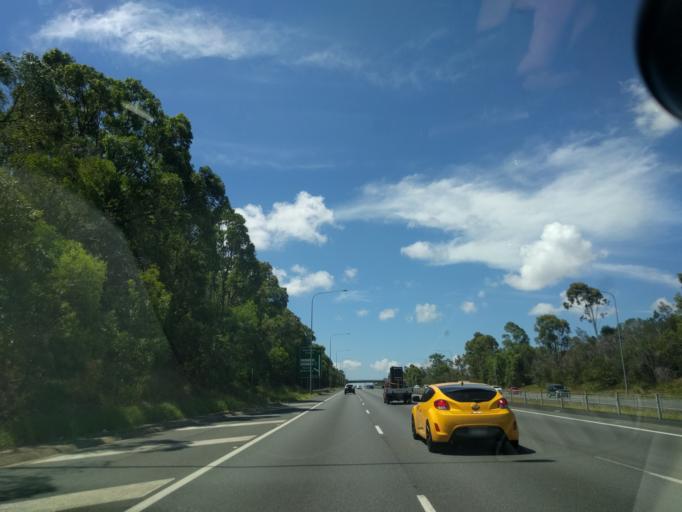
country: AU
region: Queensland
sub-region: Moreton Bay
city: Murrumba Downs
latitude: -27.2656
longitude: 153.0181
